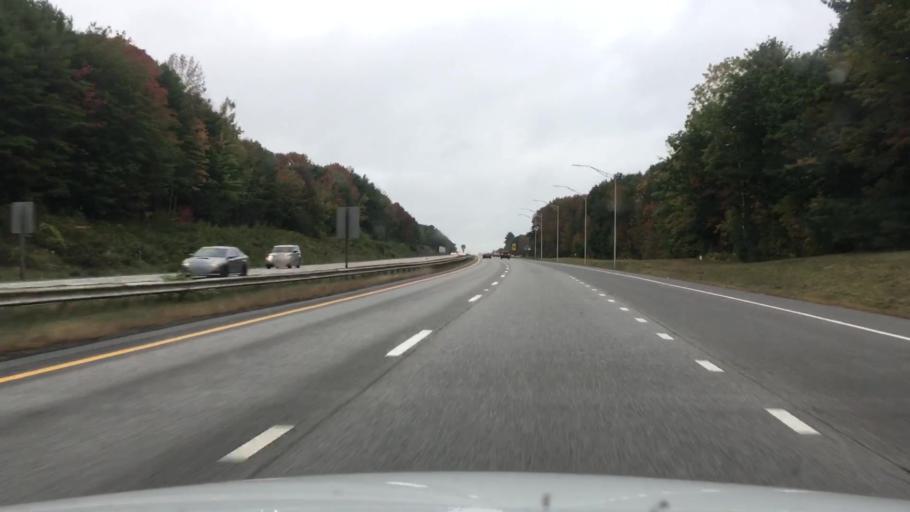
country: US
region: Maine
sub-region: Cumberland County
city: Falmouth
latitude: 43.7356
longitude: -70.3018
